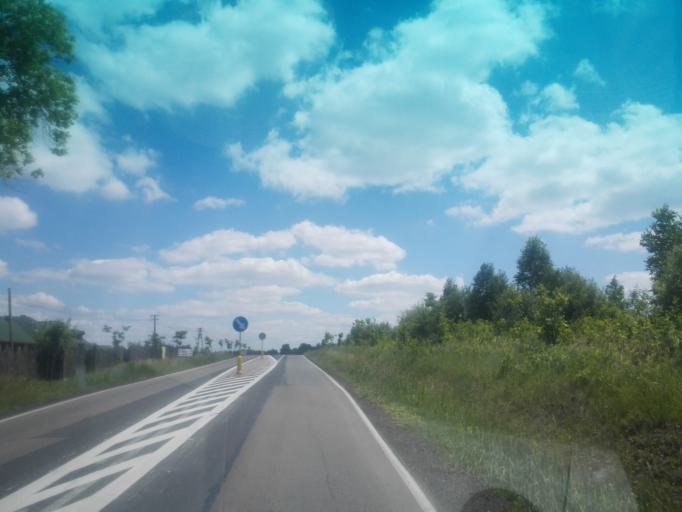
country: PL
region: Silesian Voivodeship
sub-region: Powiat czestochowski
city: Potok Zloty
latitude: 50.7311
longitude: 19.4032
